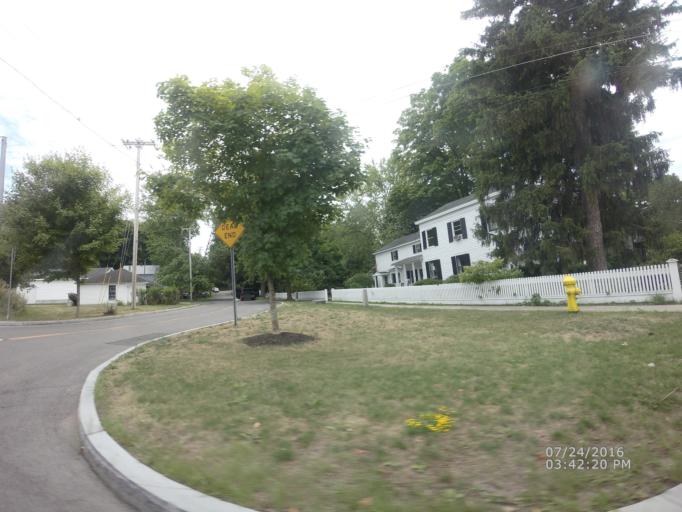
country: US
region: New York
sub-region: Onondaga County
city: Camillus
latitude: 43.0390
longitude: -76.3041
